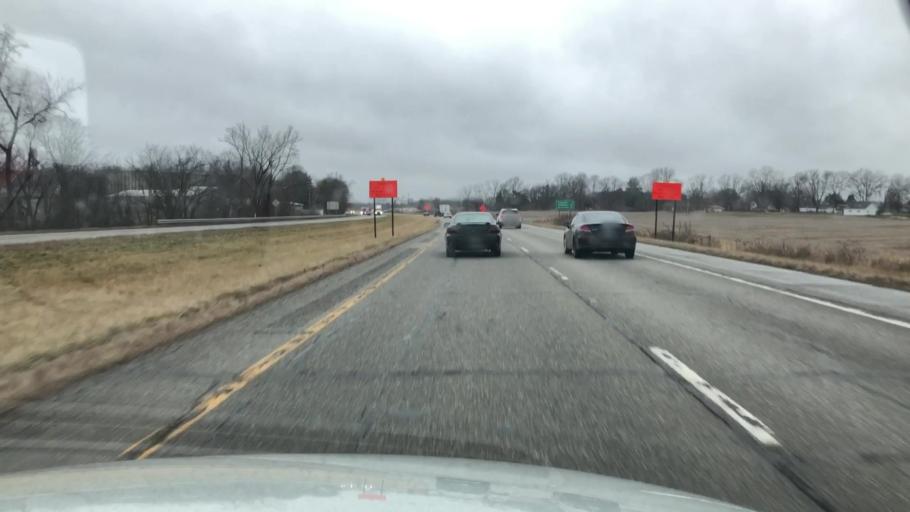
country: US
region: Indiana
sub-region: Marshall County
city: Plymouth
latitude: 41.3571
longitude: -86.2835
